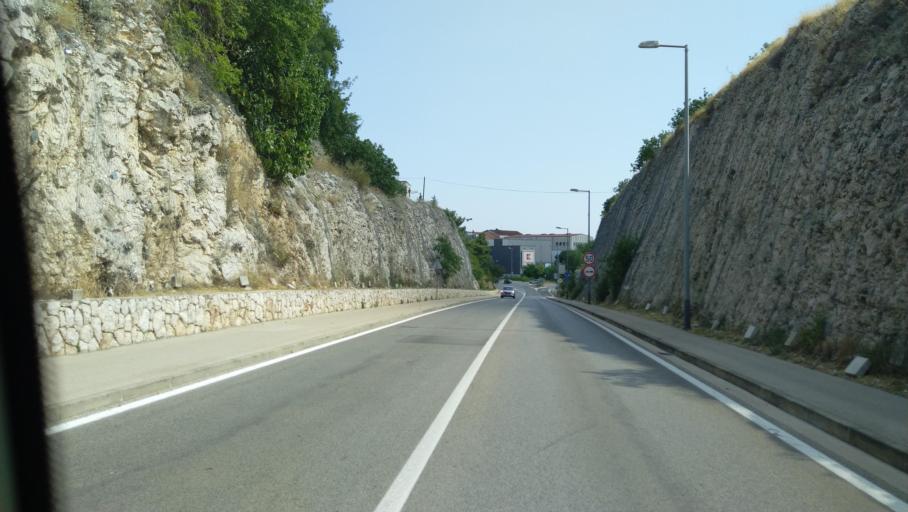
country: HR
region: Sibensko-Kniniska
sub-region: Grad Sibenik
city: Sibenik
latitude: 43.7256
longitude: 15.9040
